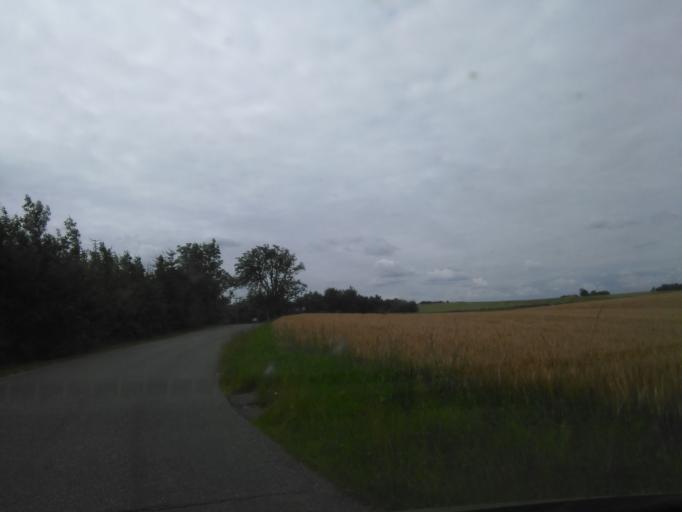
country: DK
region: Central Jutland
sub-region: Arhus Kommune
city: Solbjerg
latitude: 56.0181
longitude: 10.0724
